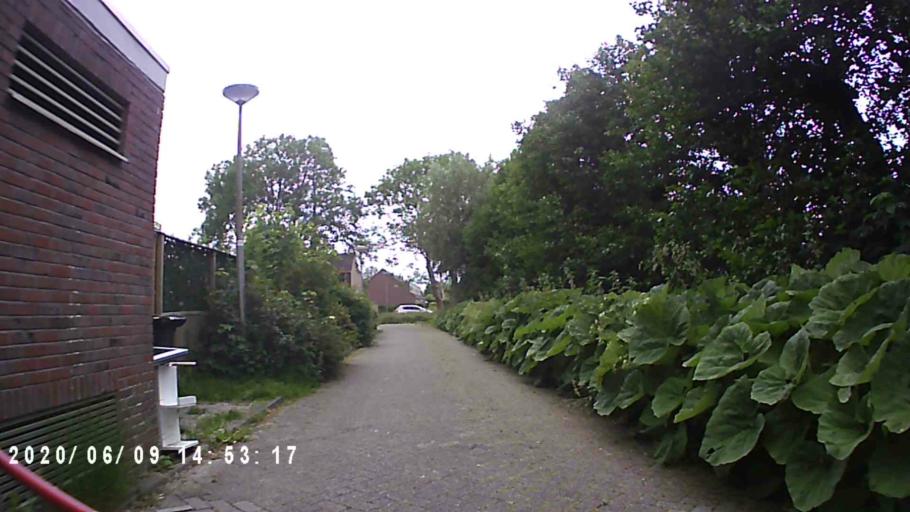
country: NL
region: Groningen
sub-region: Gemeente Winsum
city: Winsum
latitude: 53.3311
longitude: 6.5231
